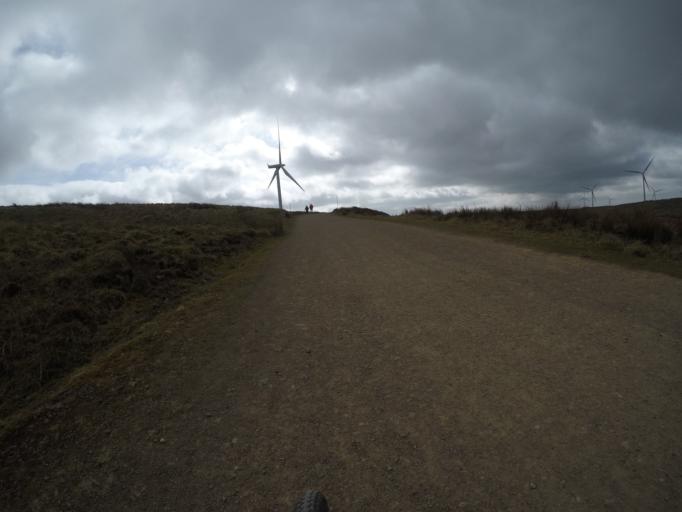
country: GB
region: Scotland
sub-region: East Renfrewshire
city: Eaglesham
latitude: 55.7054
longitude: -4.3238
